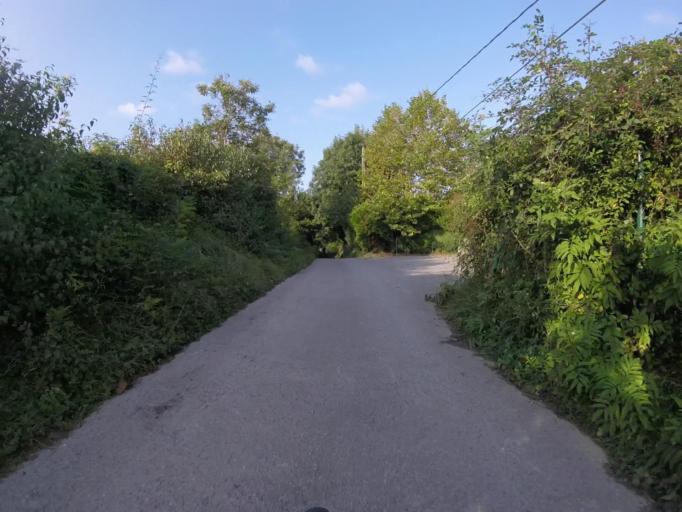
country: ES
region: Basque Country
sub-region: Provincia de Guipuzcoa
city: Fuenterrabia
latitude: 43.3594
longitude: -1.8095
